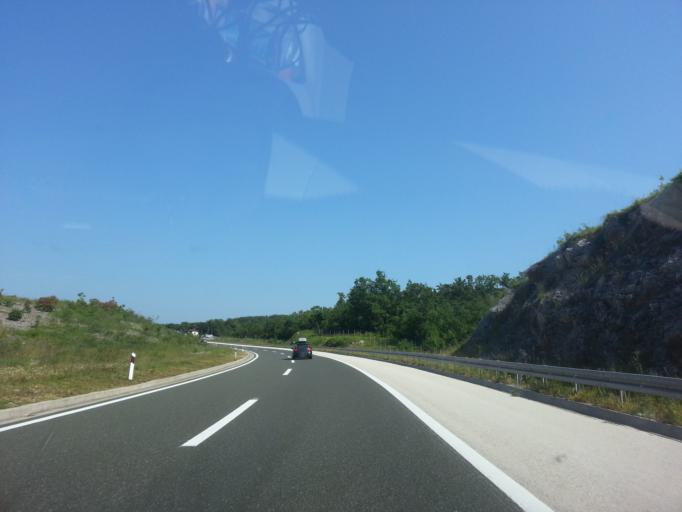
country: HR
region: Primorsko-Goranska
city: Matulji
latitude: 45.4243
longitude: 14.2990
